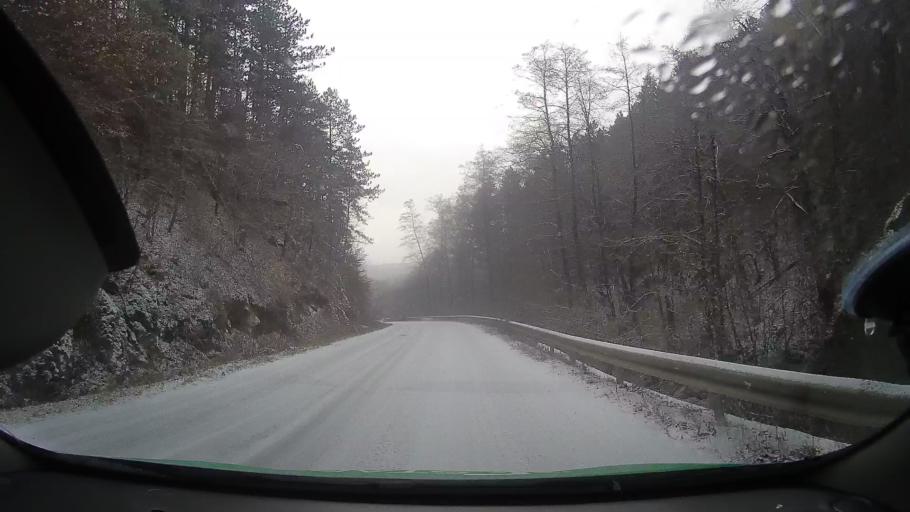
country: RO
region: Alba
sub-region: Comuna Livezile
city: Livezile
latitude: 46.3706
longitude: 23.5877
